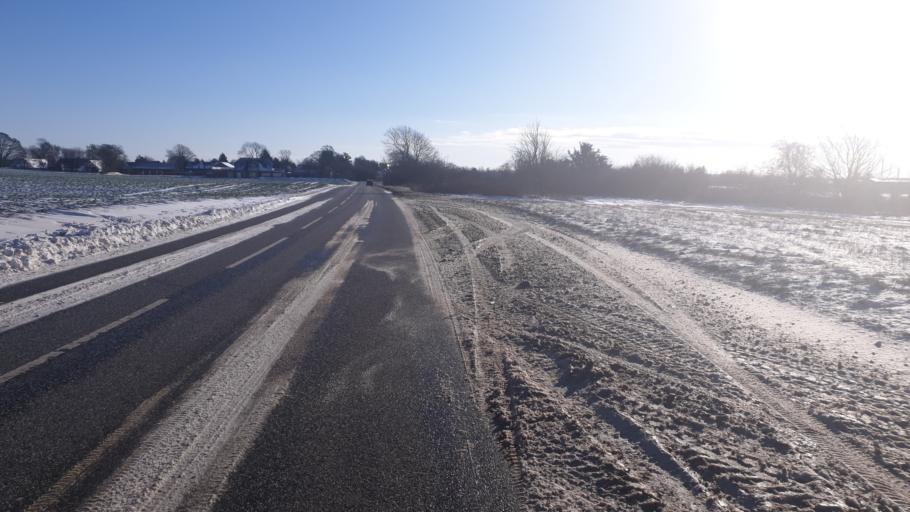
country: DK
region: Central Jutland
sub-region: Hedensted Kommune
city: Hedensted
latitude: 55.7848
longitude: 9.7099
